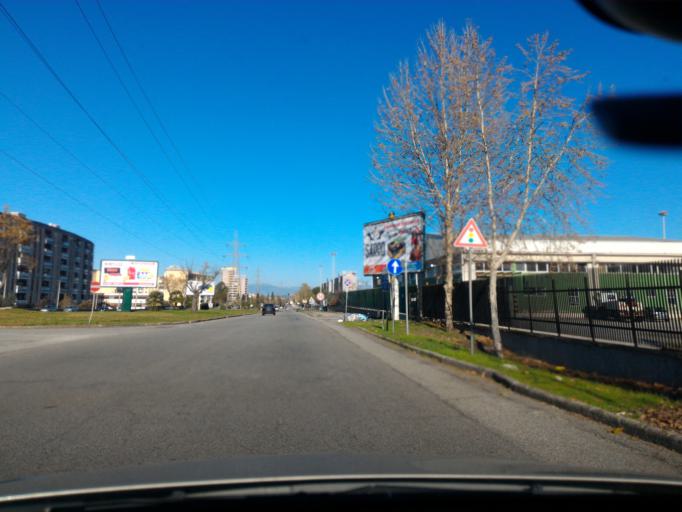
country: IT
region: Calabria
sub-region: Provincia di Cosenza
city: Cosenza
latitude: 39.3154
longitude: 16.2585
